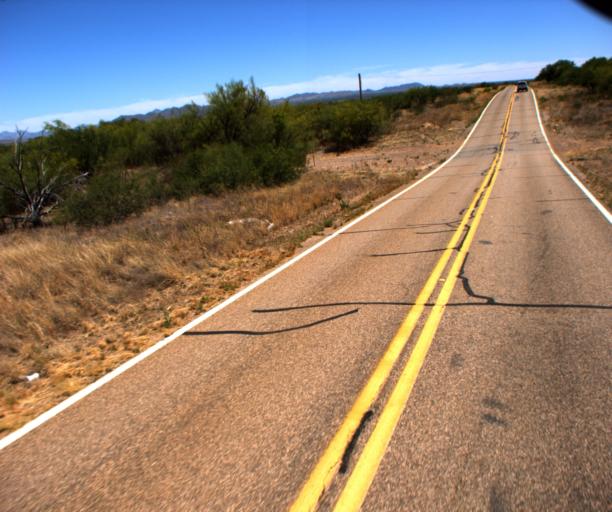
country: US
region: Arizona
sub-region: Pima County
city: Three Points
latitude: 31.6961
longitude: -111.4872
